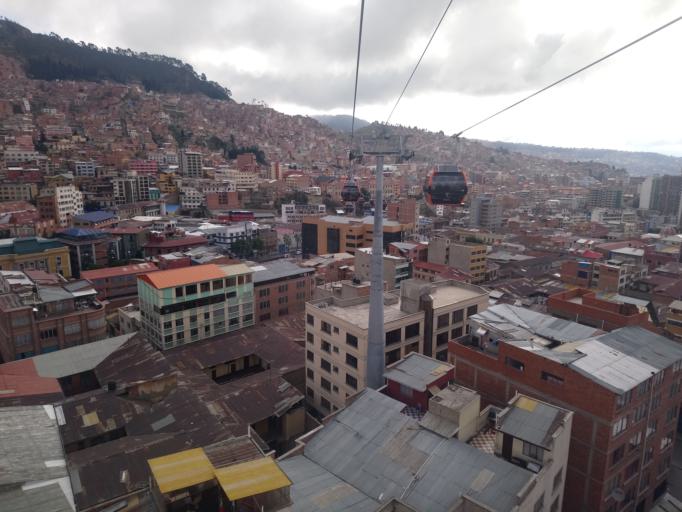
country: BO
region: La Paz
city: La Paz
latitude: -16.4915
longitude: -68.1424
